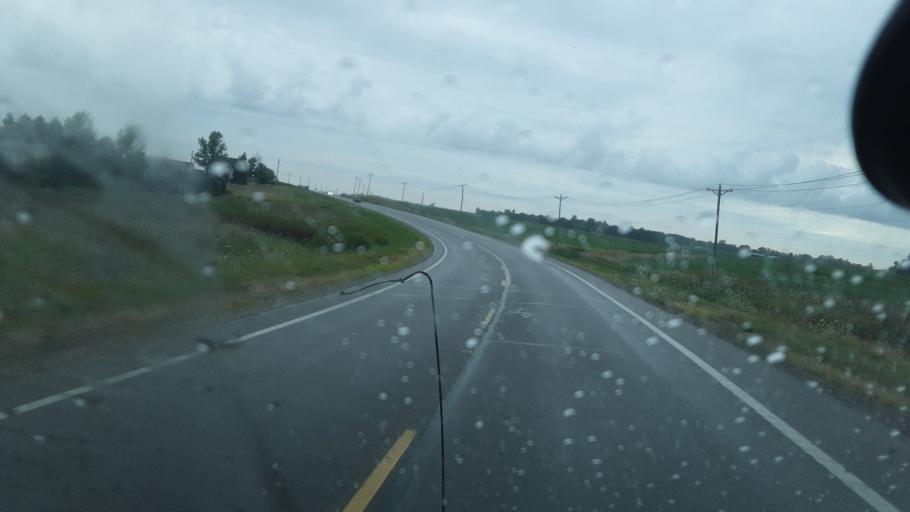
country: US
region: Ohio
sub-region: Williams County
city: Montpelier
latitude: 41.6178
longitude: -84.5530
